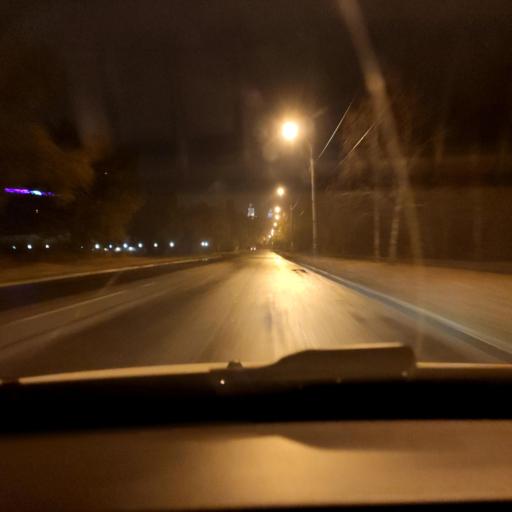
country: RU
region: Voronezj
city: Voronezh
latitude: 51.6521
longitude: 39.2119
